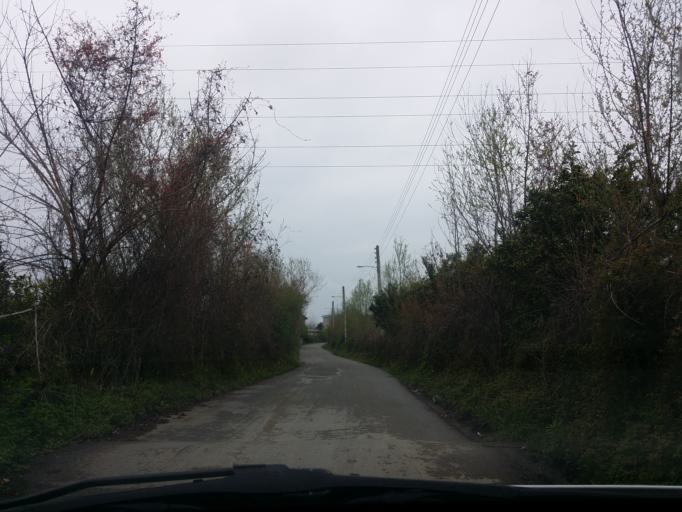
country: IR
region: Mazandaran
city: Chalus
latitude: 36.6741
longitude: 51.3790
